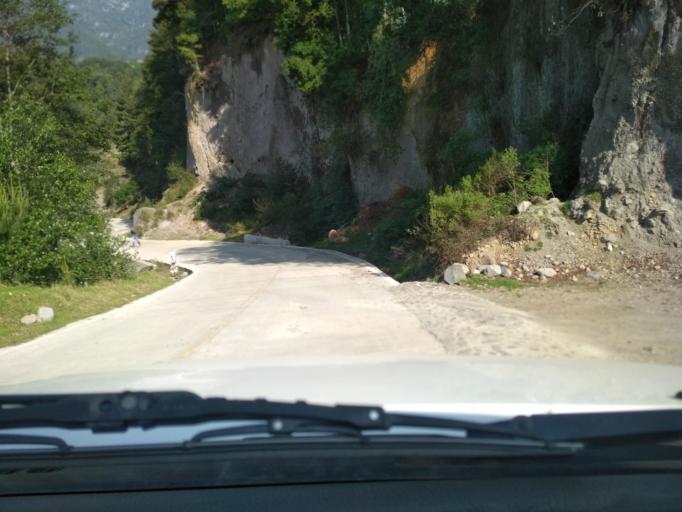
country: MX
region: Veracruz
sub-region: La Perla
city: Chilapa
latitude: 19.0020
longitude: -97.1832
